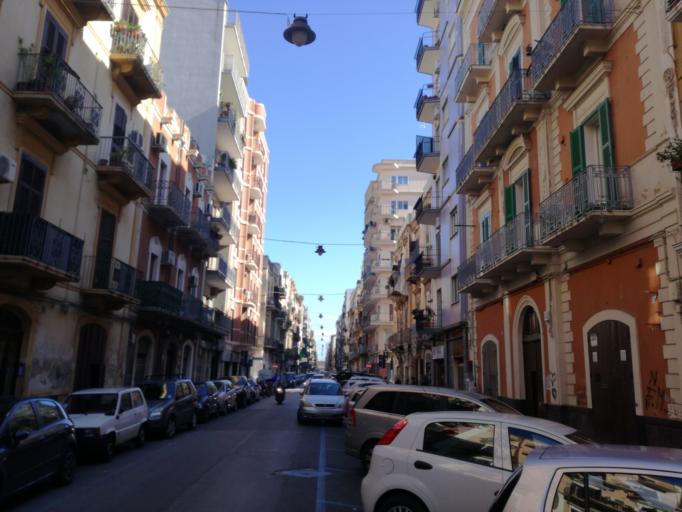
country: IT
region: Apulia
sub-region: Provincia di Bari
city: Bari
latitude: 41.1235
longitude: 16.8590
